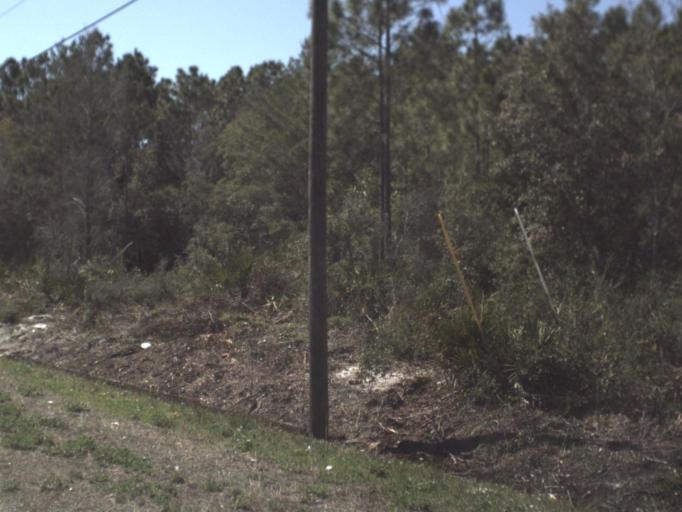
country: US
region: Florida
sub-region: Franklin County
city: Carrabelle
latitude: 29.8649
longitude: -84.6203
